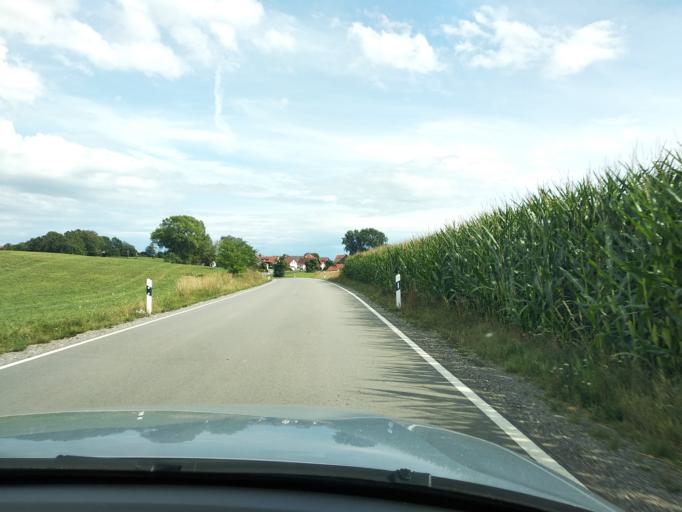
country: DE
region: Bavaria
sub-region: Swabia
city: Wolfertschwenden
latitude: 47.8628
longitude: 10.2407
